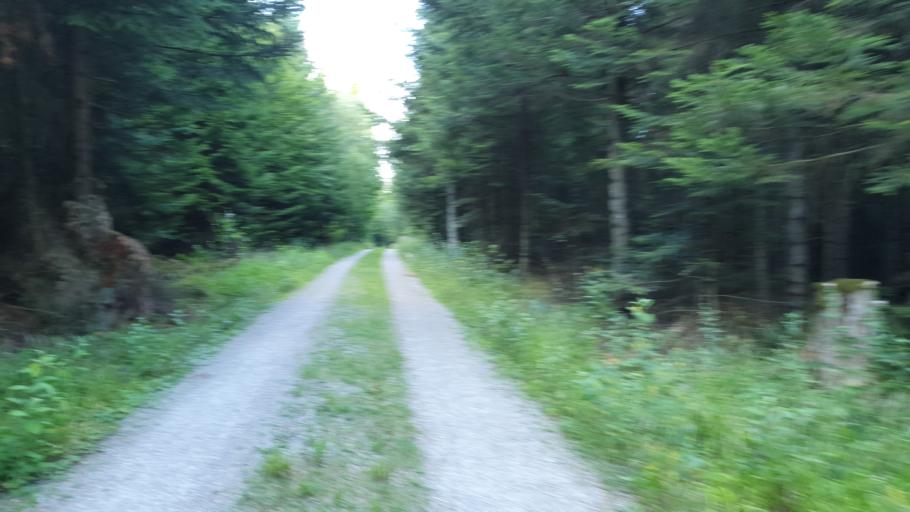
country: DE
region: Baden-Wuerttemberg
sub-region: Karlsruhe Region
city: Dornstetten
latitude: 48.5097
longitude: 8.5147
